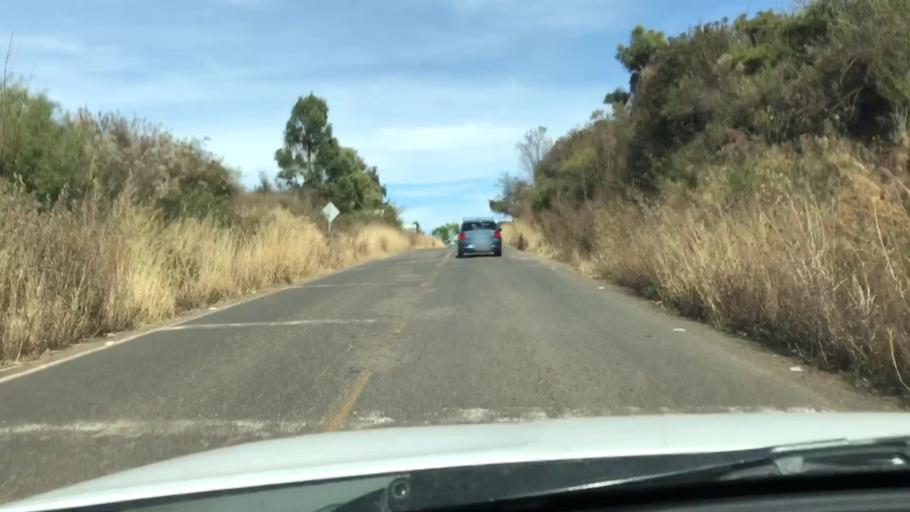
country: MX
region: Jalisco
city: Chiquilistlan
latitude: 20.1883
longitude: -103.7243
